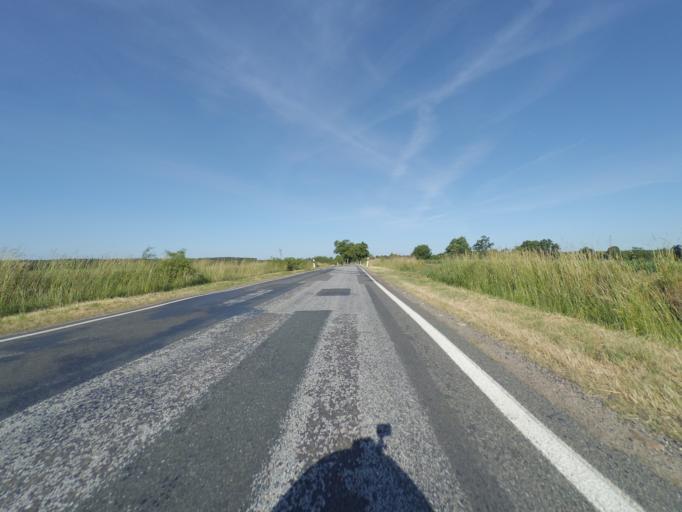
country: DE
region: Mecklenburg-Vorpommern
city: Plau am See
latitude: 53.3704
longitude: 12.1843
